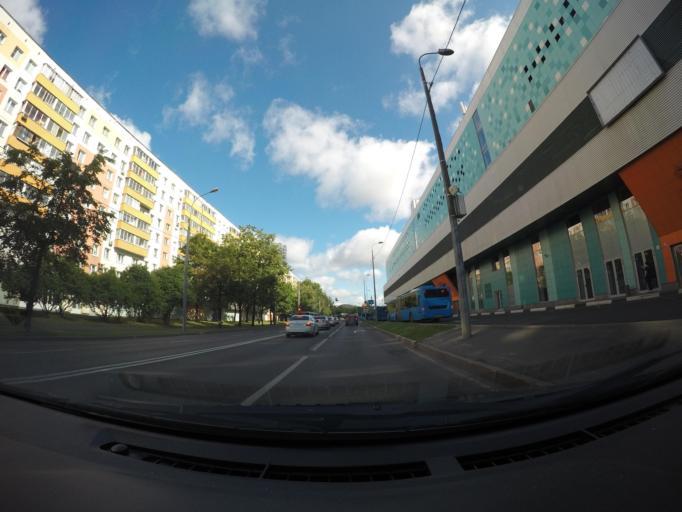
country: RU
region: Moscow
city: Khimki
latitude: 55.8624
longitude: 37.4344
